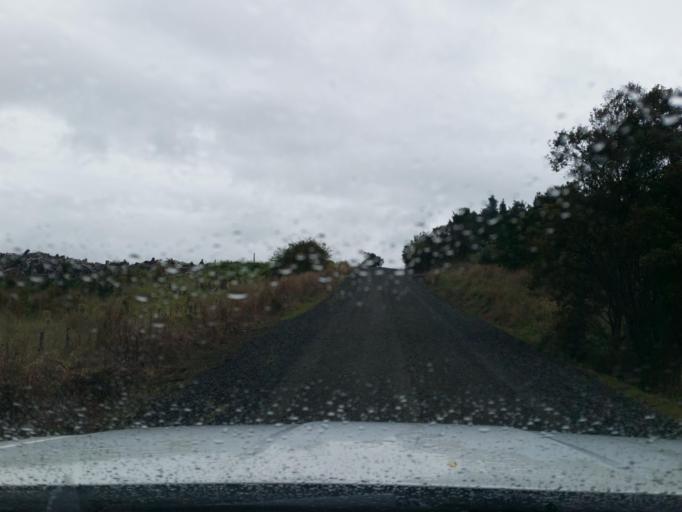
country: NZ
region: Northland
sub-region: Kaipara District
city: Dargaville
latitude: -35.8678
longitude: 173.8847
